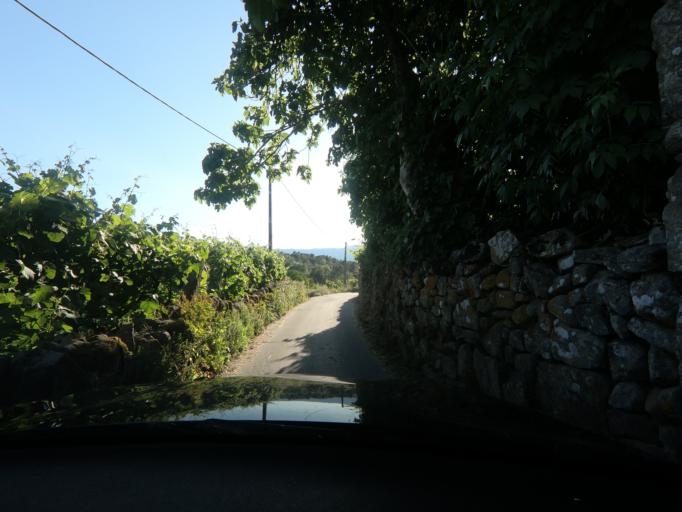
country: PT
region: Vila Real
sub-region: Vila Real
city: Vila Real
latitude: 41.3134
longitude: -7.7030
